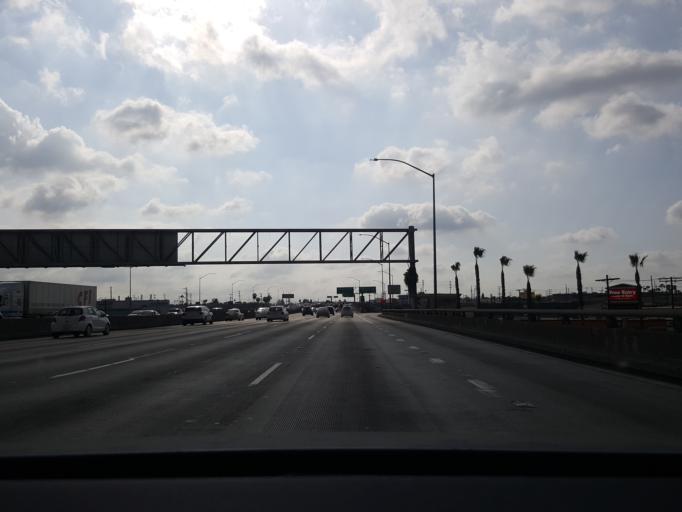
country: US
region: California
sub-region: Los Angeles County
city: Los Angeles
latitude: 34.0268
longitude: -118.2347
